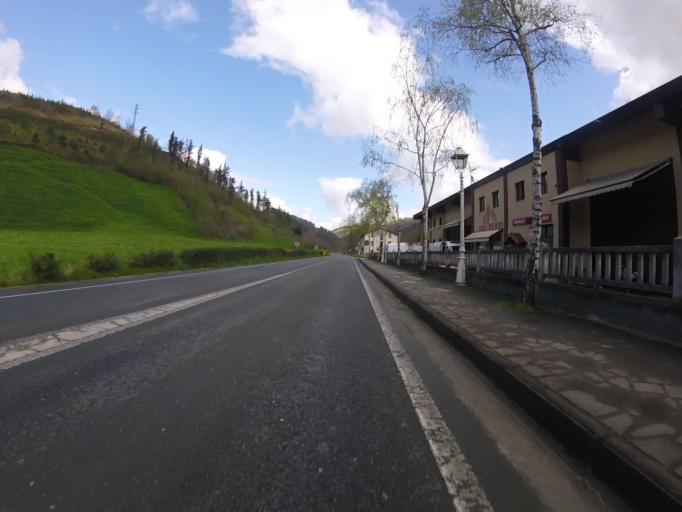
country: ES
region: Basque Country
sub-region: Provincia de Guipuzcoa
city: Amezqueta
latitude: 43.0559
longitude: -2.0883
